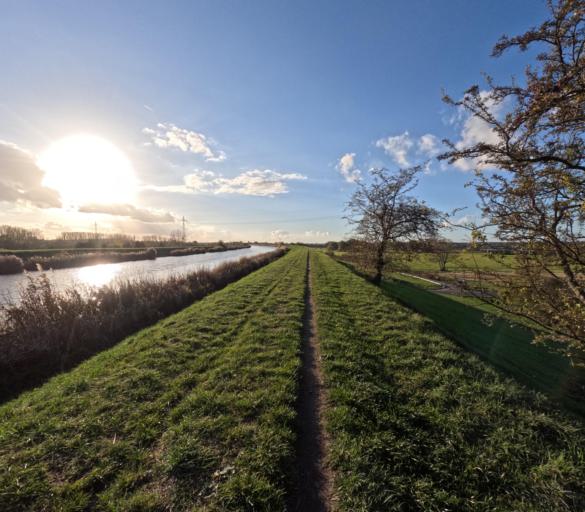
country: DE
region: Saxony-Anhalt
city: Gunthersdorf
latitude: 51.3586
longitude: 12.2082
